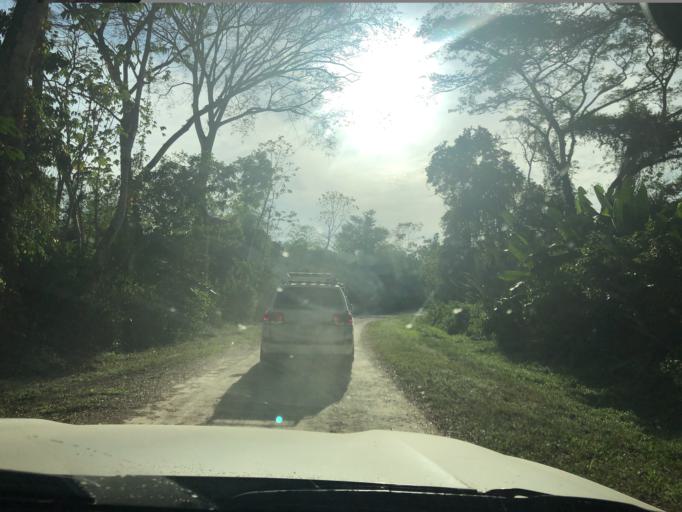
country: NI
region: Rivas
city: Cardenas
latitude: 11.1278
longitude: -85.3063
